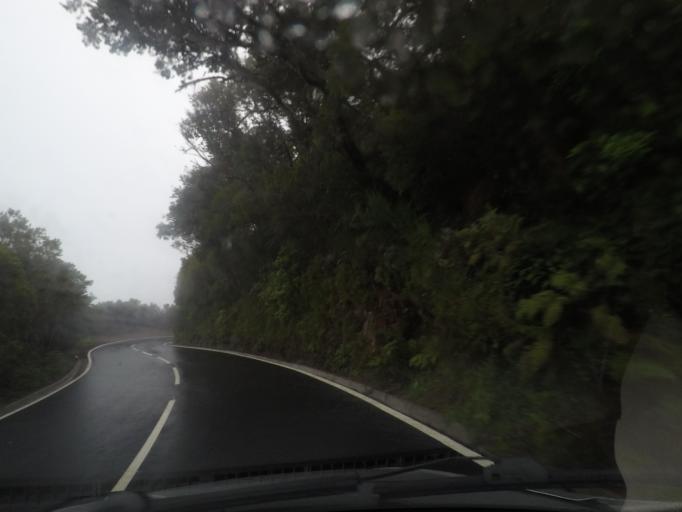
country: PT
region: Madeira
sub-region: Santana
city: Santana
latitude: 32.7675
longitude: -16.9150
